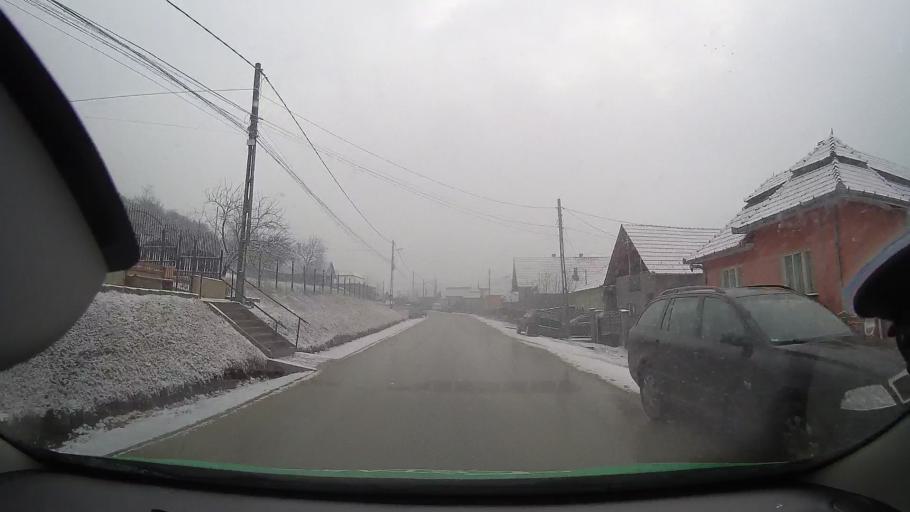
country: RO
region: Alba
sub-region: Comuna Lopadea Noua
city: Lopadea Noua
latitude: 46.2954
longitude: 23.8152
